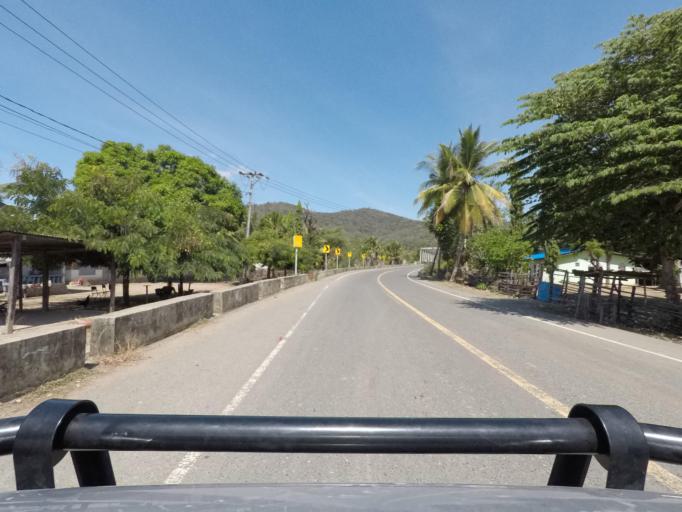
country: TL
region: Liquica
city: Maubara
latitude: -8.7943
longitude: 125.1016
